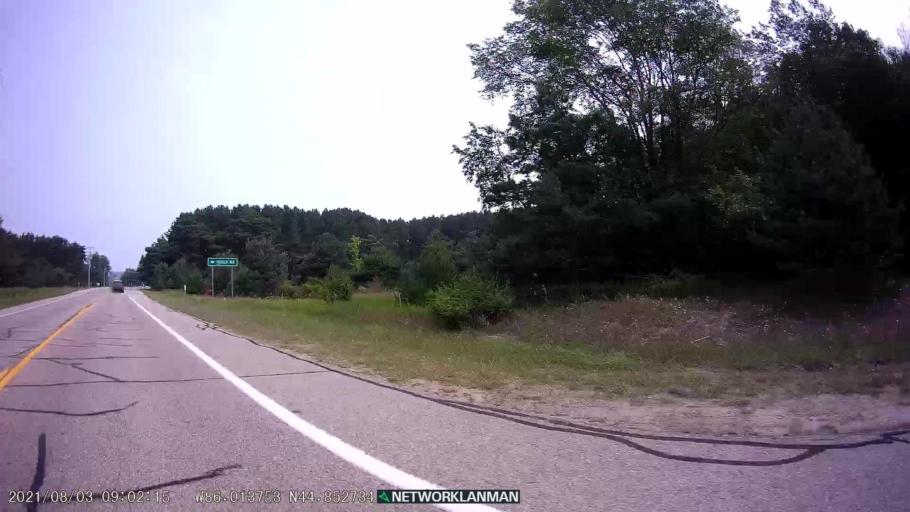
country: US
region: Michigan
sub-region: Benzie County
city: Beulah
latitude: 44.8524
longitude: -86.0140
